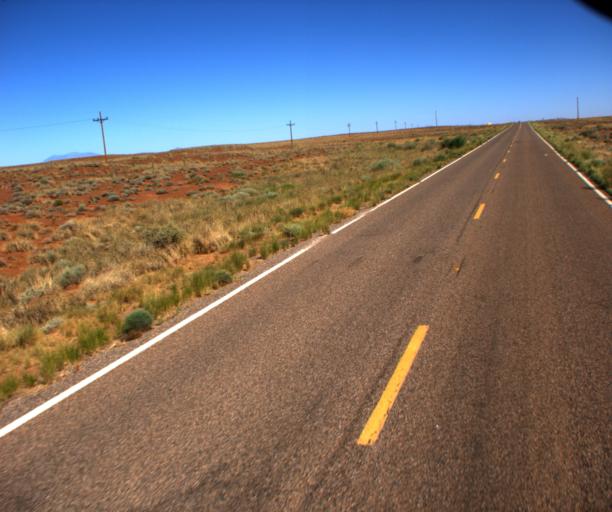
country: US
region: Arizona
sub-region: Coconino County
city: LeChee
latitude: 35.1783
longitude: -110.9273
